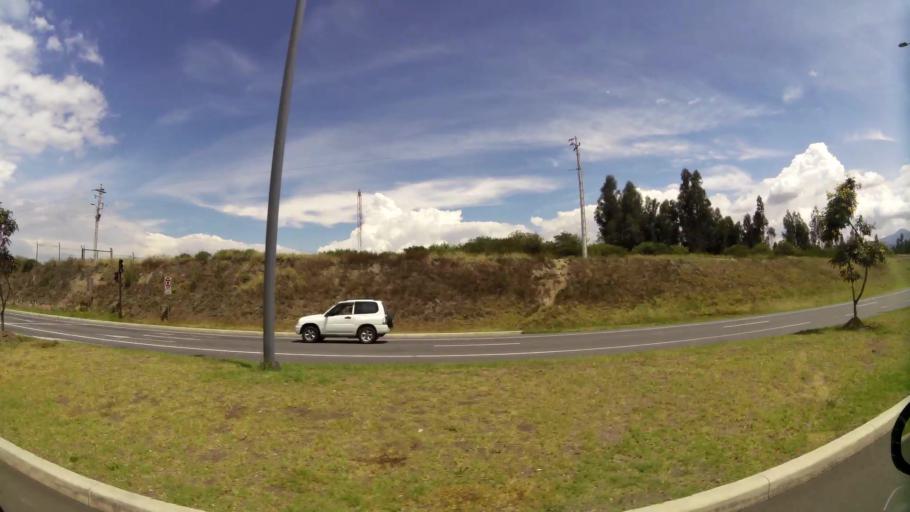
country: EC
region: Pichincha
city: Quito
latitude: -0.1535
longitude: -78.3500
